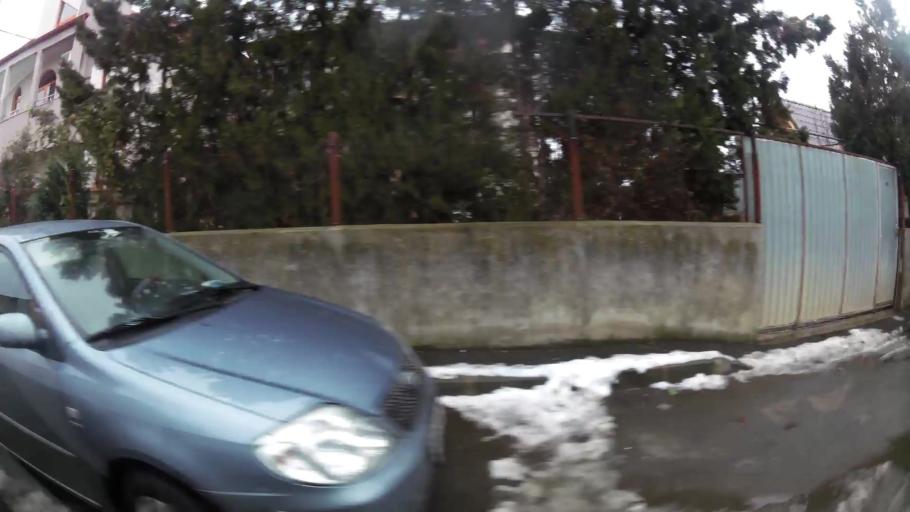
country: RO
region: Ilfov
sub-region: Comuna Popesti-Leordeni
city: Popesti-Leordeni
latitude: 44.4049
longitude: 26.1730
